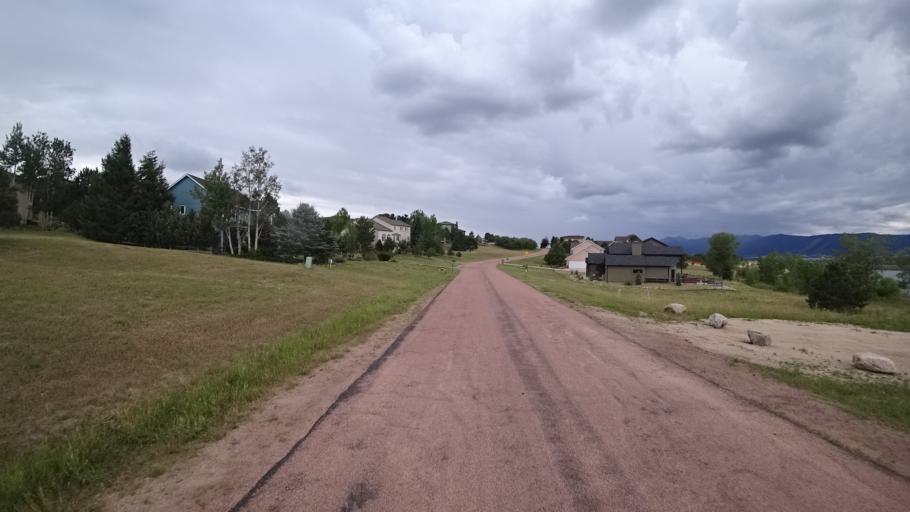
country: US
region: Colorado
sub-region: El Paso County
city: Woodmoor
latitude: 39.1007
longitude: -104.8536
